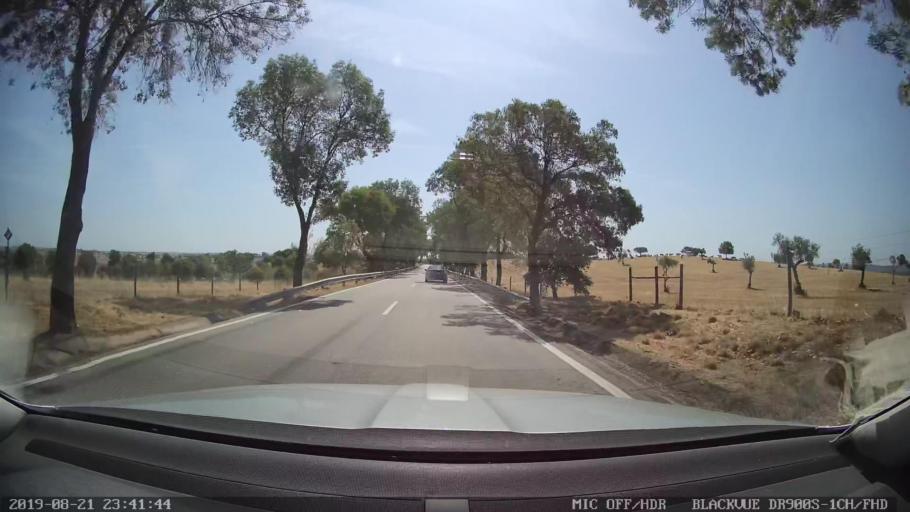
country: PT
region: Castelo Branco
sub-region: Idanha-A-Nova
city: Idanha-a-Nova
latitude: 39.8626
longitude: -7.3190
